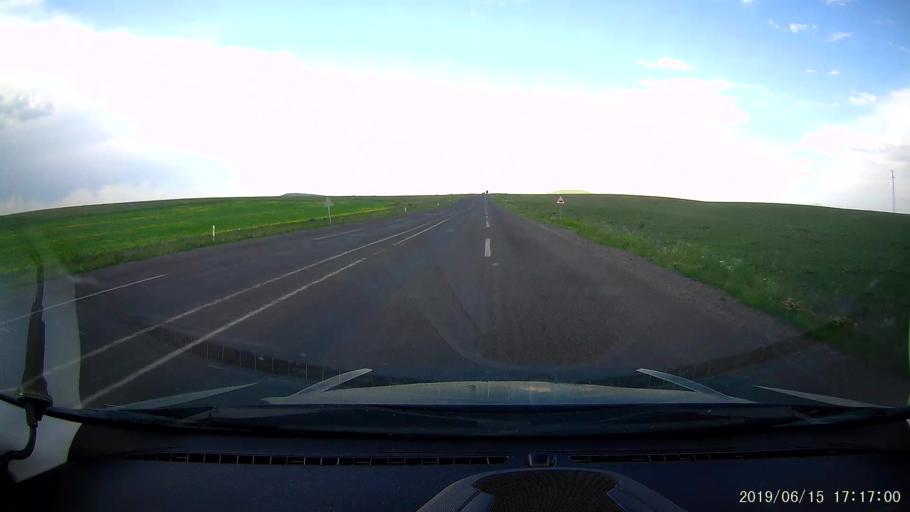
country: TR
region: Kars
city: Kars
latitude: 40.6143
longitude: 43.2296
